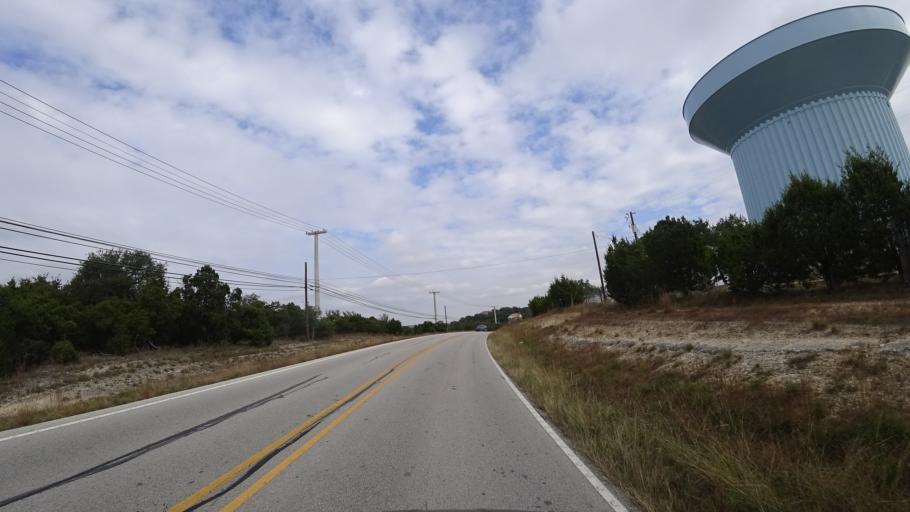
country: US
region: Texas
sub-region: Travis County
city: Shady Hollow
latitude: 30.2025
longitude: -97.9183
